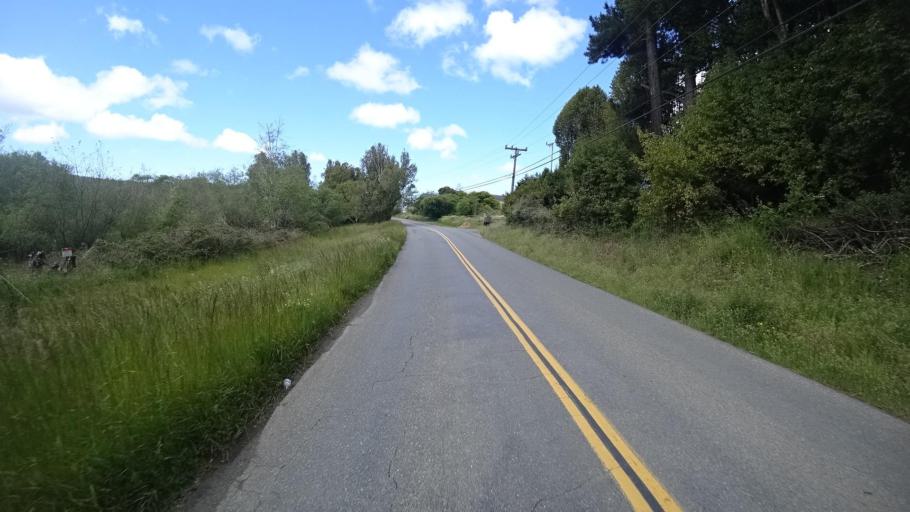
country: US
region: California
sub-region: Humboldt County
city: Blue Lake
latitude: 40.9004
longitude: -124.0108
